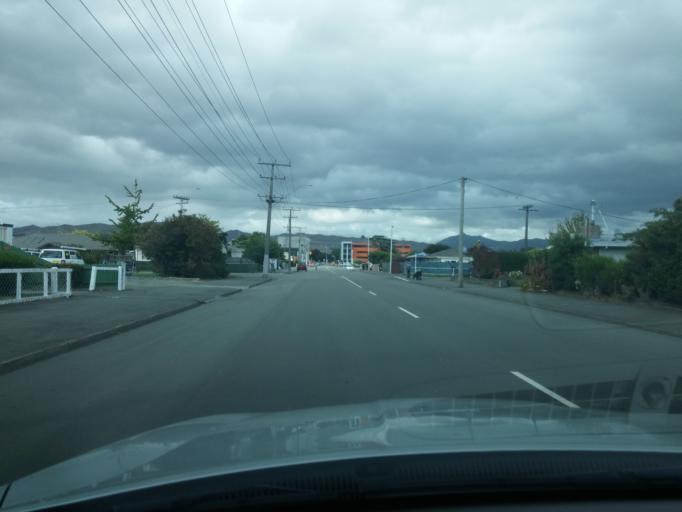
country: NZ
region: Marlborough
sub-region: Marlborough District
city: Blenheim
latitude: -41.5058
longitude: 173.9559
